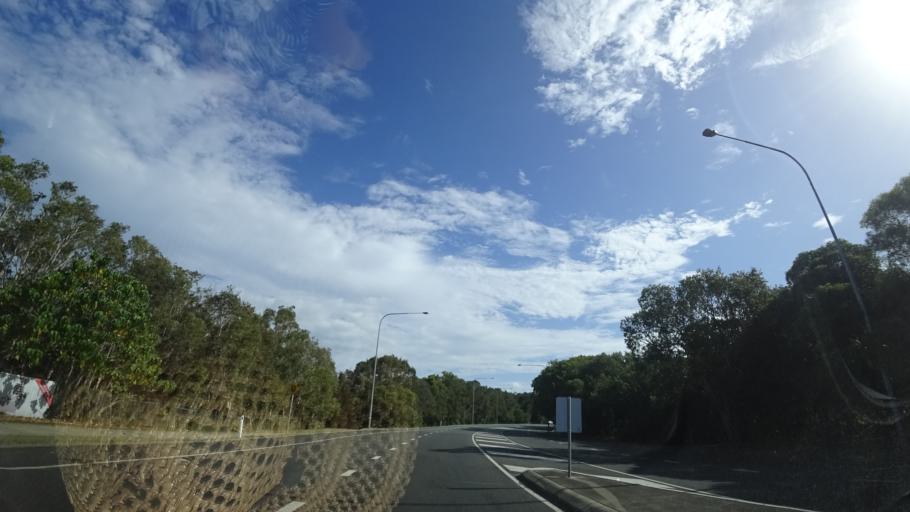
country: AU
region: Queensland
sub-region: Sunshine Coast
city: Coolum Beach
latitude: -26.5607
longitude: 153.0953
